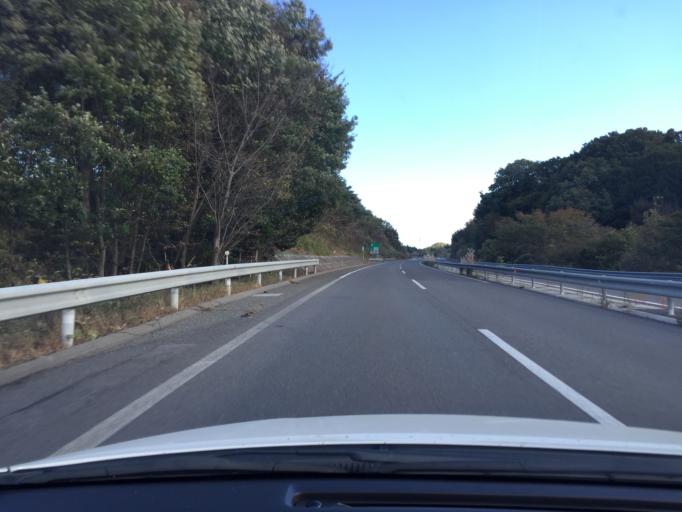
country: JP
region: Fukushima
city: Miharu
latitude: 37.4345
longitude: 140.4721
